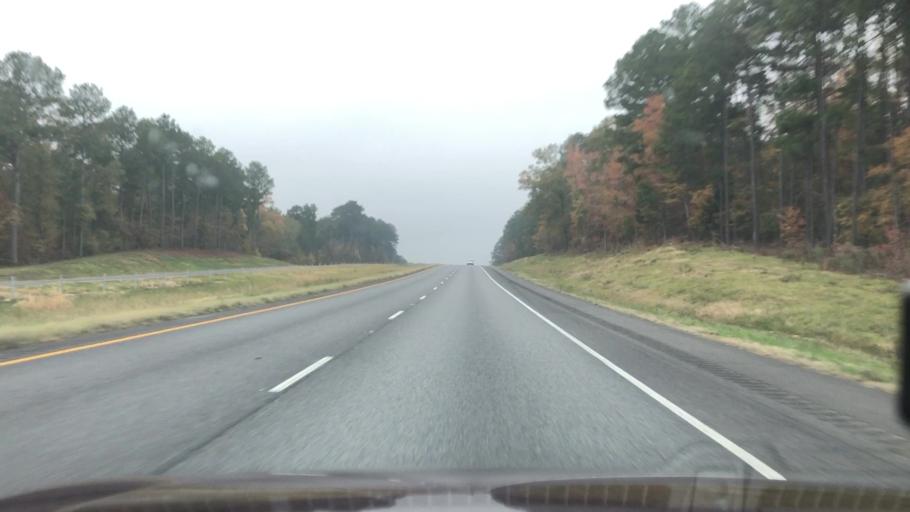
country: US
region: Louisiana
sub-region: Lincoln Parish
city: Ruston
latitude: 32.5234
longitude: -92.4230
